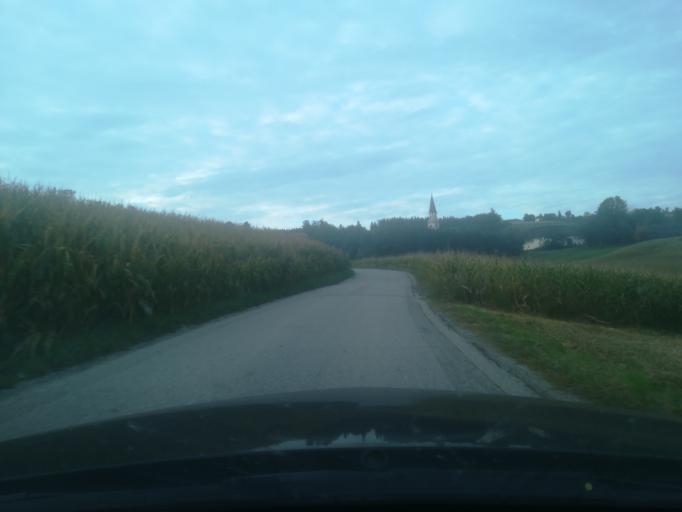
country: AT
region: Upper Austria
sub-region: Wels-Land
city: Buchkirchen
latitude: 48.2524
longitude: 14.0488
